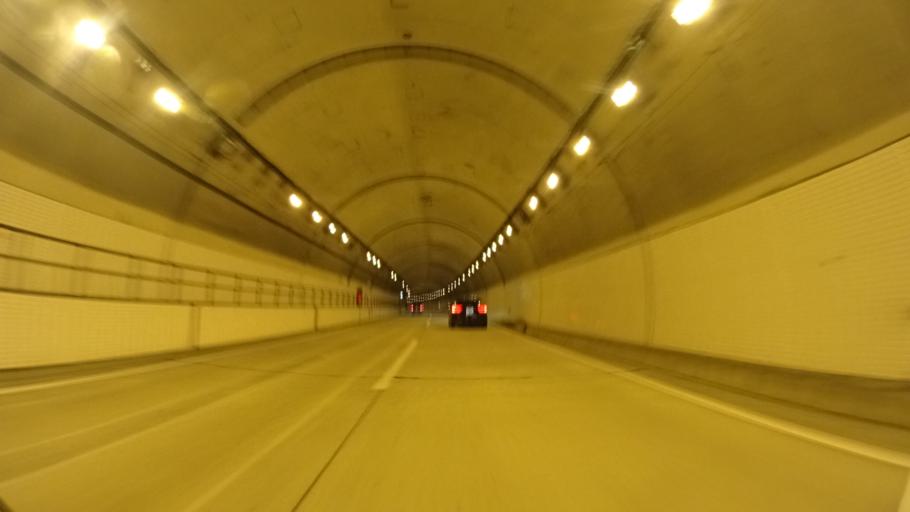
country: JP
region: Ehime
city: Niihama
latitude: 33.9167
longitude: 133.2992
